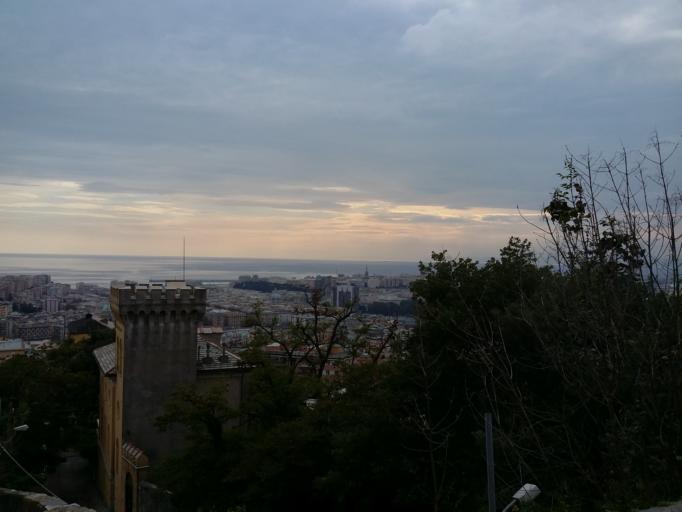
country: IT
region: Liguria
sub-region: Provincia di Genova
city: Genoa
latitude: 44.4127
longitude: 8.9632
